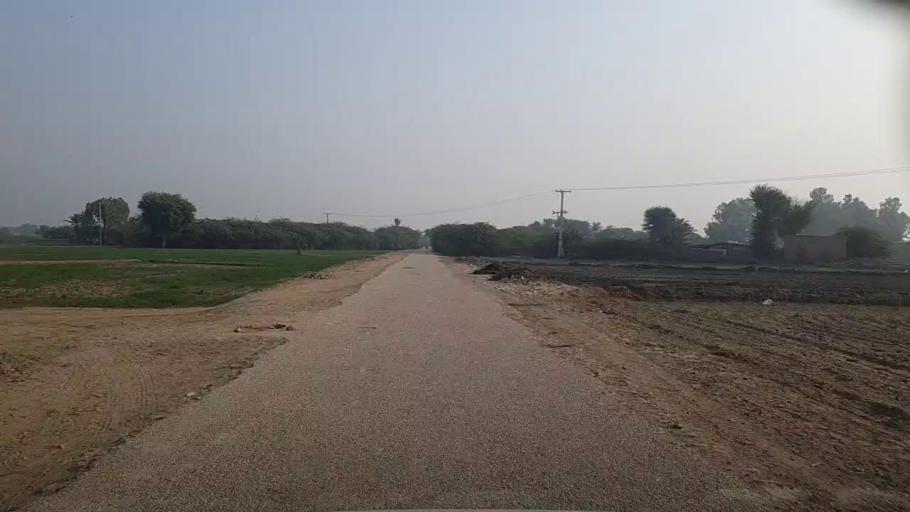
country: PK
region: Sindh
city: Kandiari
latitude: 27.0400
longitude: 68.4784
